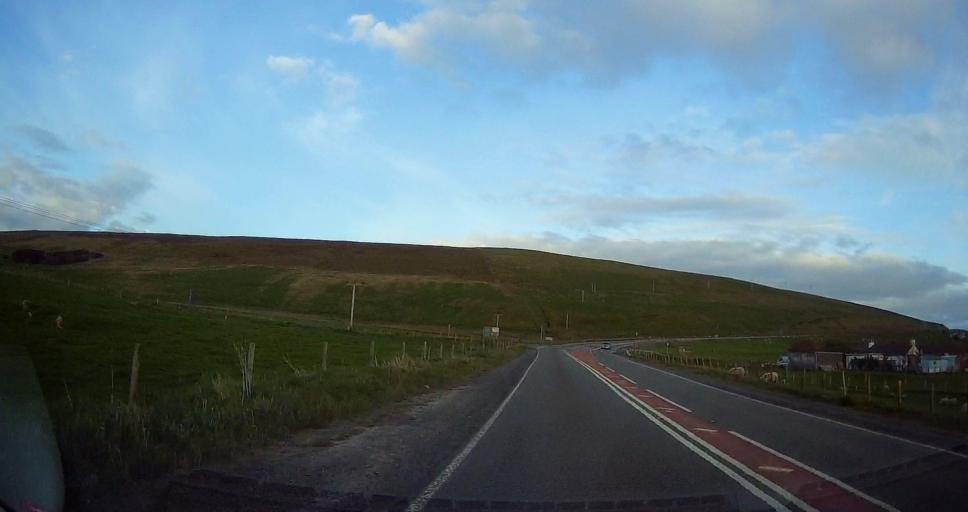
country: GB
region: Scotland
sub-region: Shetland Islands
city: Lerwick
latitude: 60.1870
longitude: -1.2284
